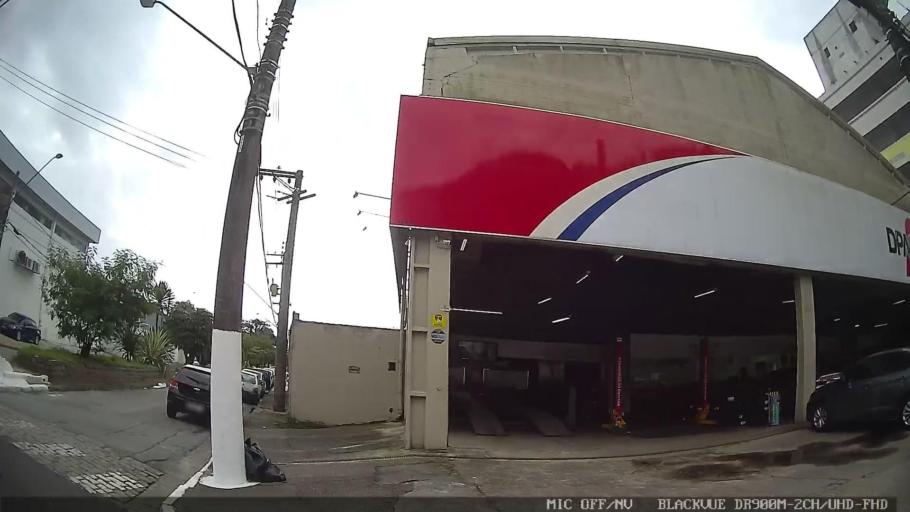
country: BR
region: Sao Paulo
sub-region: Guaruja
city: Guaruja
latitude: -23.9914
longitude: -46.2692
